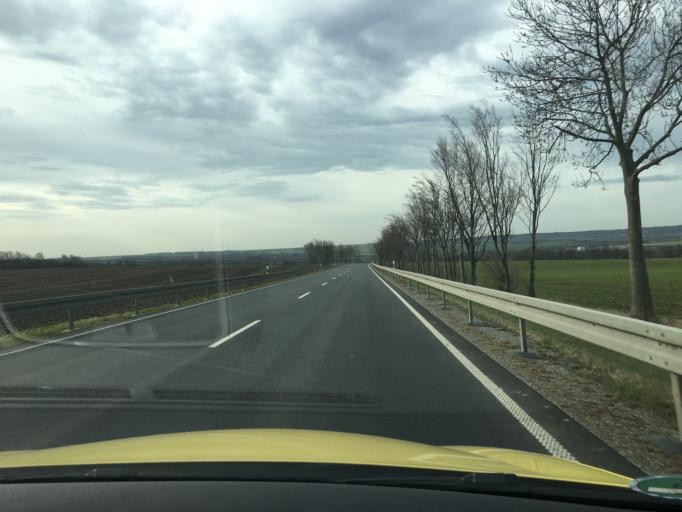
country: DE
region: Thuringia
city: Buttelstedt
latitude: 51.0883
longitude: 11.3485
